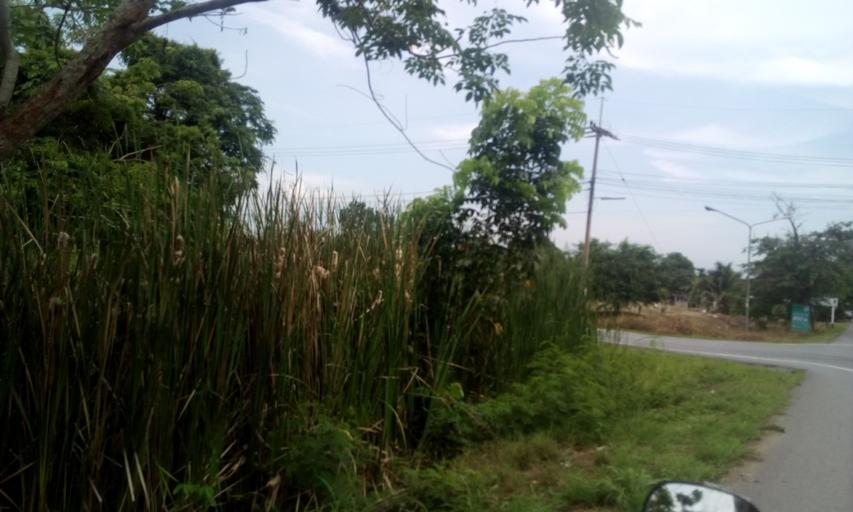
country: TH
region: Pathum Thani
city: Ban Lam Luk Ka
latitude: 14.0064
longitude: 100.8422
